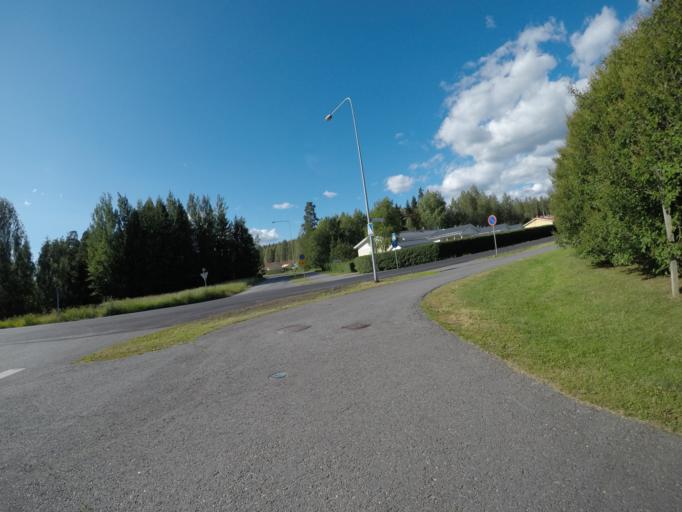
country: FI
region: Haeme
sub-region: Haemeenlinna
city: Haemeenlinna
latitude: 61.0197
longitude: 24.5179
